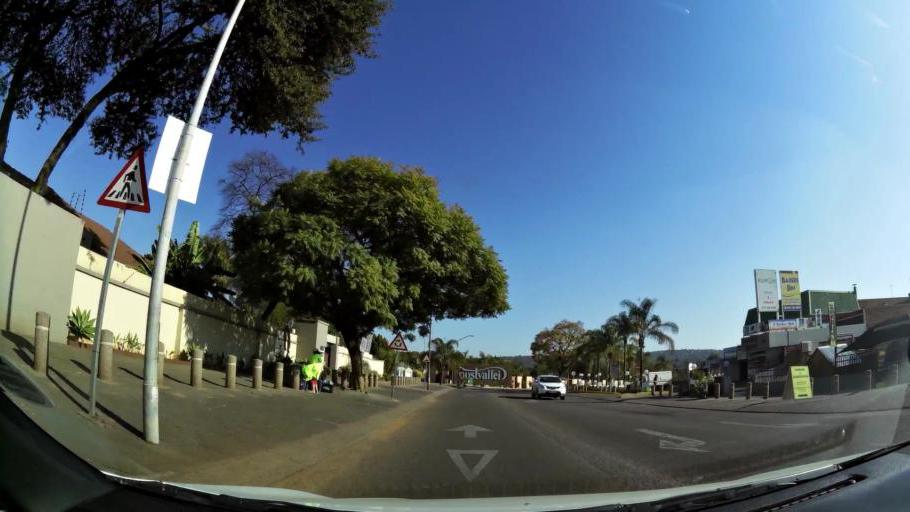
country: ZA
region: Gauteng
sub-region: City of Tshwane Metropolitan Municipality
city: Pretoria
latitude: -25.7948
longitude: 28.3019
